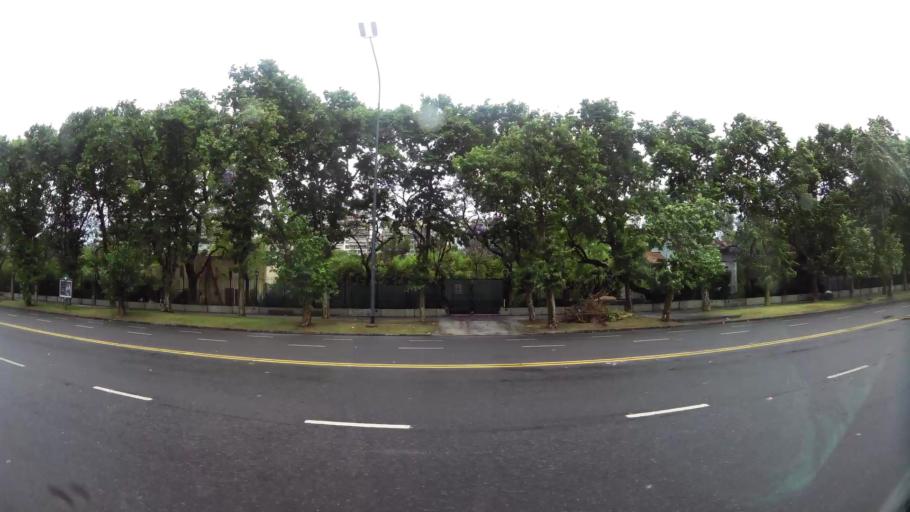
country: AR
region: Buenos Aires F.D.
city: Colegiales
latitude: -34.5764
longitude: -58.4165
